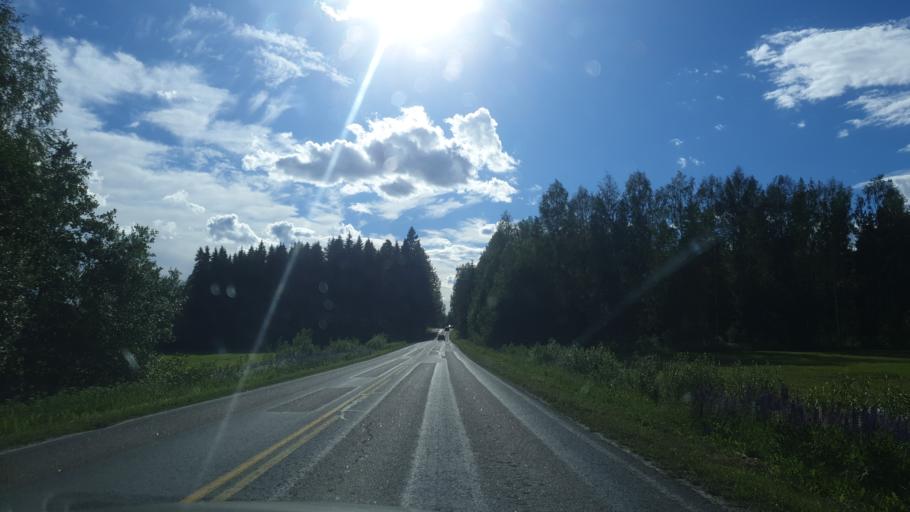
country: FI
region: Southern Savonia
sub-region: Mikkeli
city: Pertunmaa
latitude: 61.5234
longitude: 26.5197
